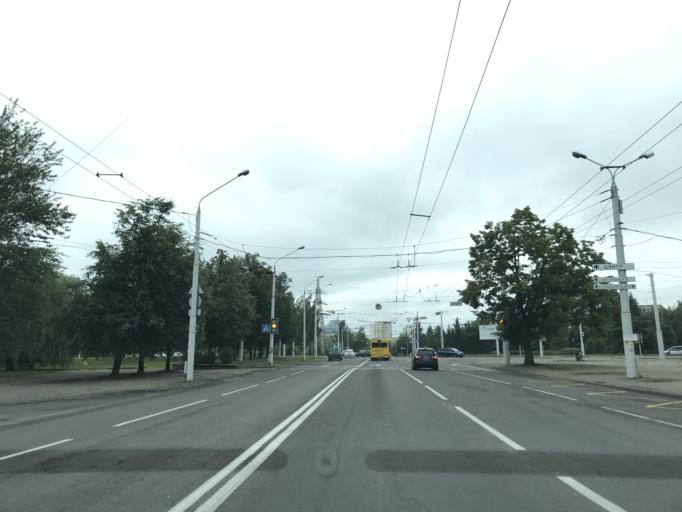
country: BY
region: Minsk
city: Borovlyany
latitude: 53.9435
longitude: 27.6428
